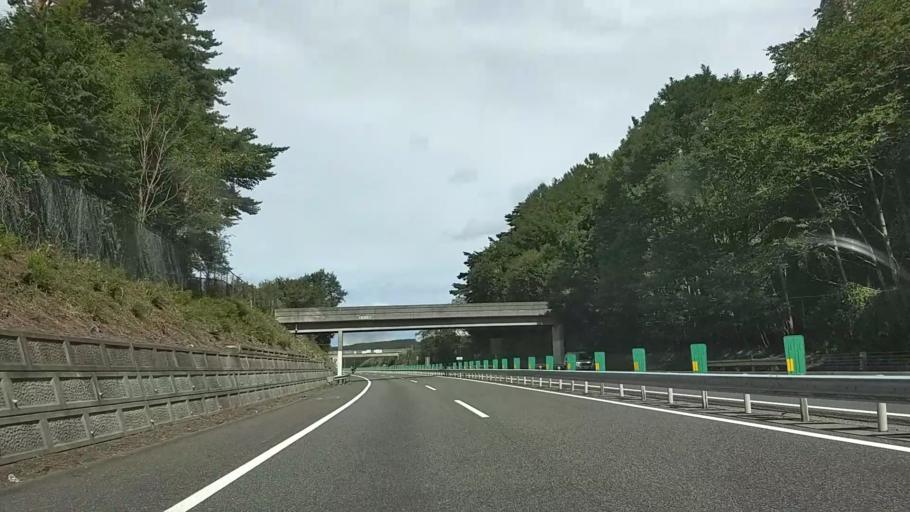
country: JP
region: Nagano
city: Chino
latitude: 35.8777
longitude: 138.3041
